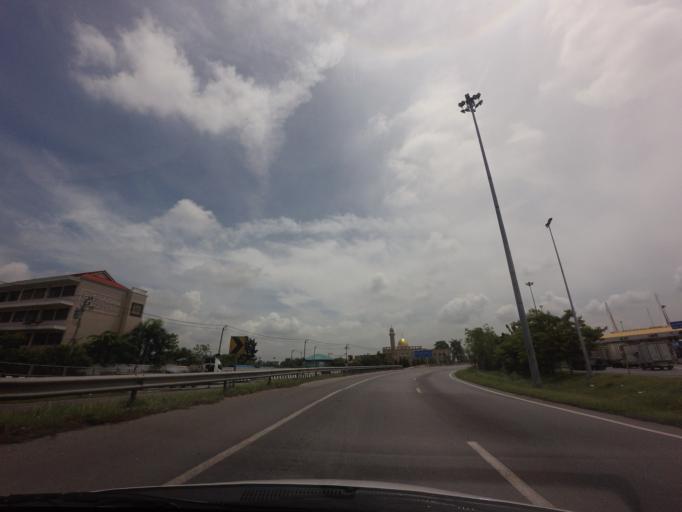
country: TH
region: Bangkok
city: Thung Khru
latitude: 13.6269
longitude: 100.5220
